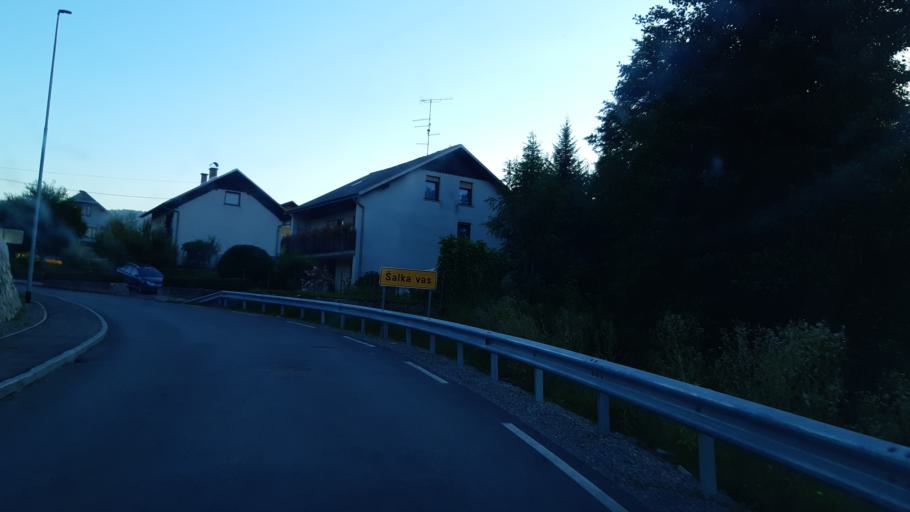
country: SI
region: Kocevje
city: Kocevje
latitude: 45.6546
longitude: 14.8816
